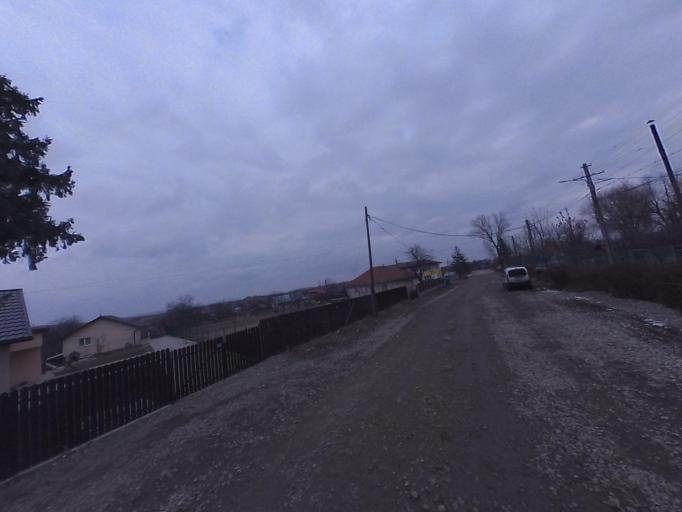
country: RO
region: Iasi
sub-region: Comuna Popricani
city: Popricani
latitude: 47.2919
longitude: 27.5045
